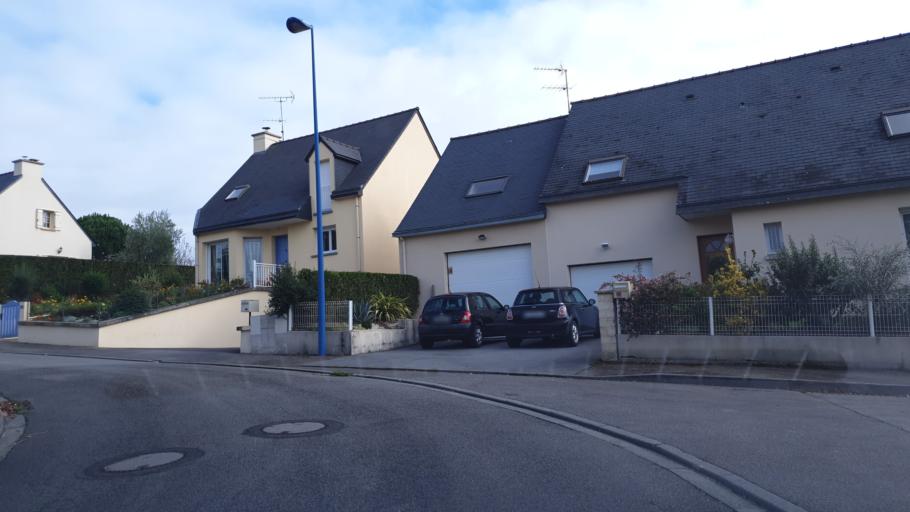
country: FR
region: Brittany
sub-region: Departement d'Ille-et-Vilaine
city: Janze
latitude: 47.9637
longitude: -1.4889
